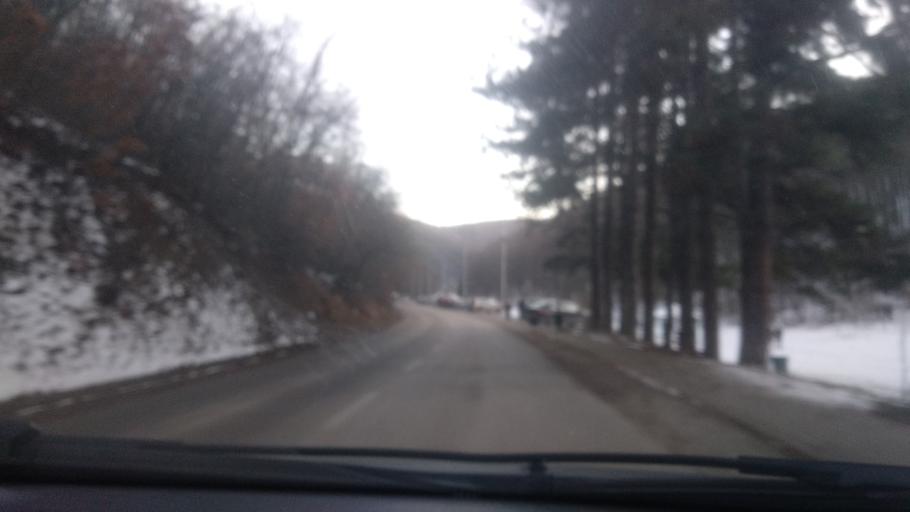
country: XK
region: Pristina
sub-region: Komuna e Prishtines
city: Pristina
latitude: 42.6736
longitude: 21.2147
